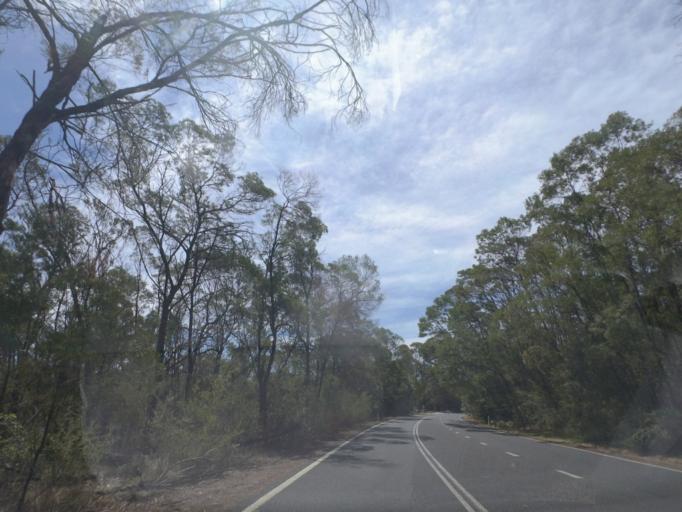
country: AU
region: New South Wales
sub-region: Wingecarribee
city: Colo Vale
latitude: -34.3923
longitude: 150.5307
